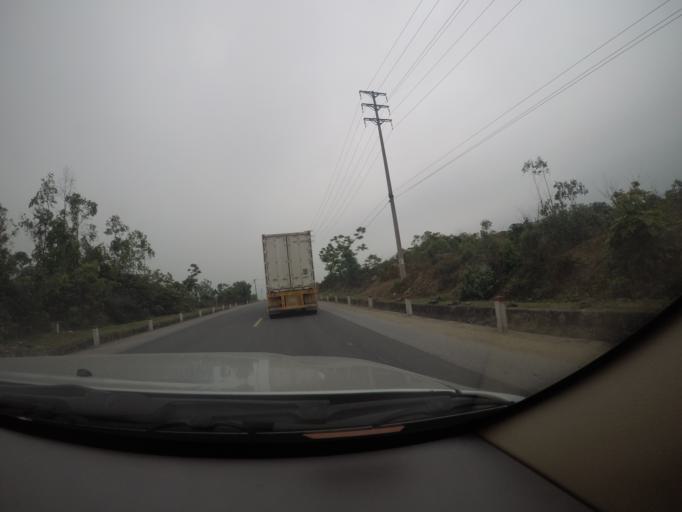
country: VN
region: Ha Tinh
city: Ky Anh
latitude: 18.0162
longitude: 106.3923
